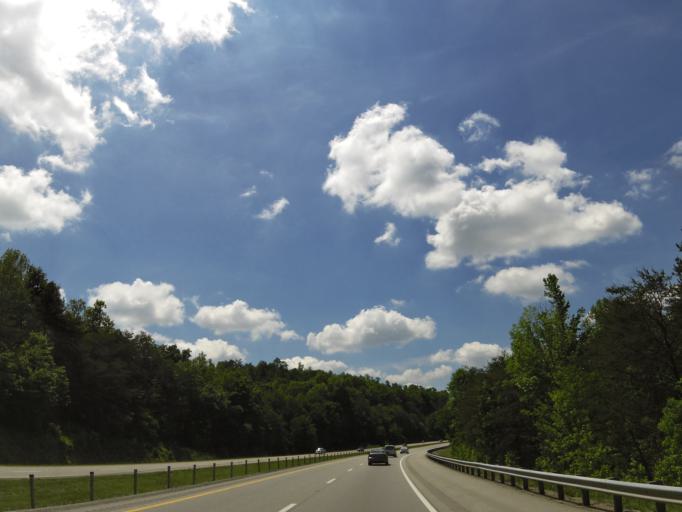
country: US
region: Kentucky
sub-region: Whitley County
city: Corbin
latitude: 36.8702
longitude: -84.1477
